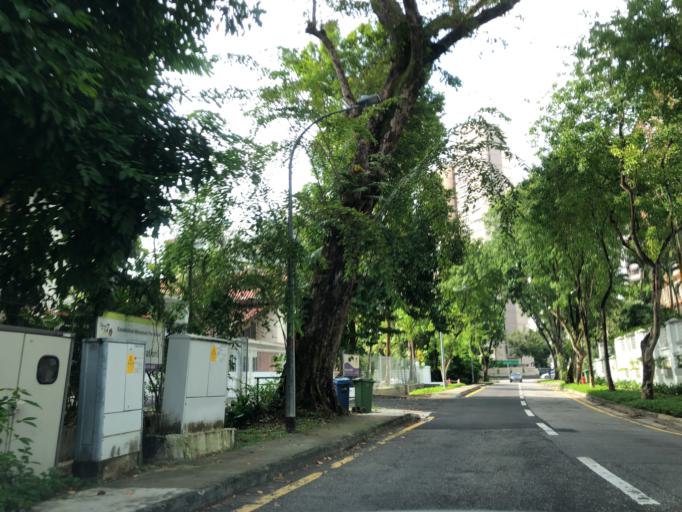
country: SG
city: Singapore
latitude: 1.3152
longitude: 103.8342
